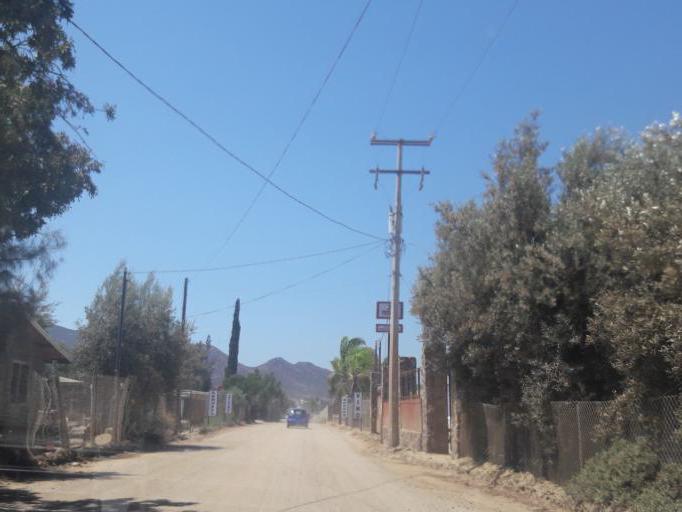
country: MX
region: Baja California
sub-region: Ensenada
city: Rancho Verde
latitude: 32.0795
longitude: -116.6205
